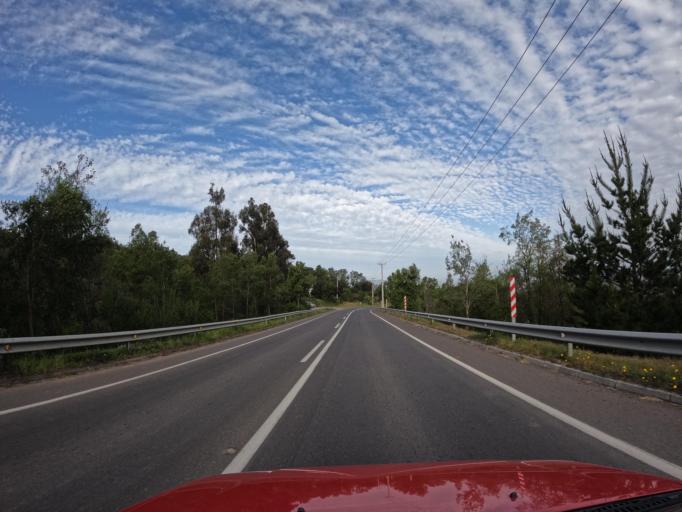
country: CL
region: Valparaiso
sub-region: San Antonio Province
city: San Antonio
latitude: -34.0490
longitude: -71.6093
